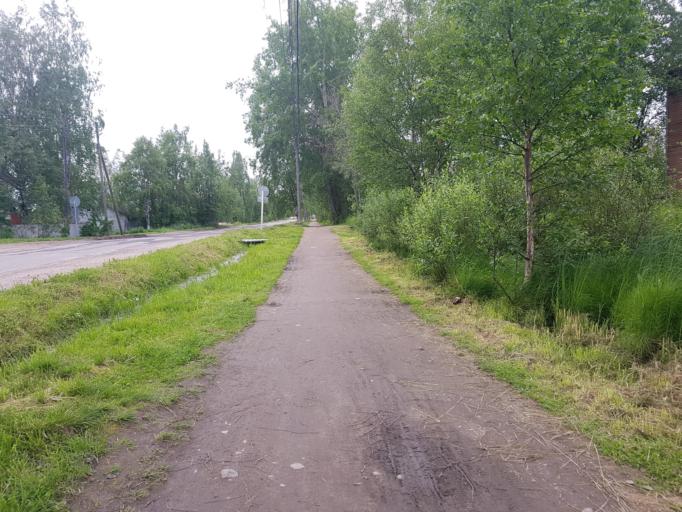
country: RU
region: Republic of Karelia
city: Kalevala
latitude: 65.2028
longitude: 31.1749
